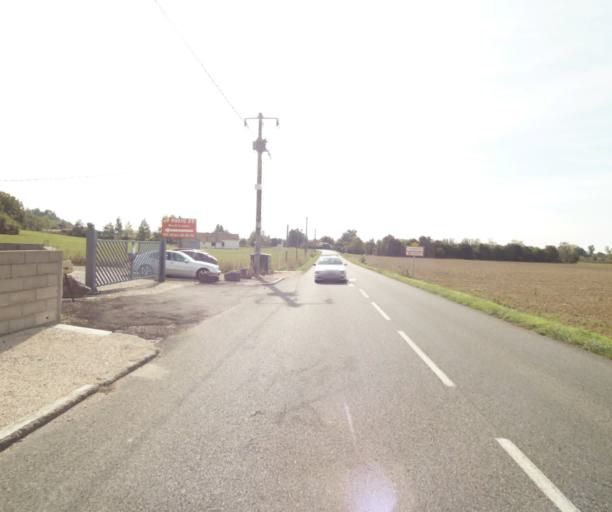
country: FR
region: Midi-Pyrenees
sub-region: Departement du Tarn-et-Garonne
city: Corbarieu
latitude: 43.9514
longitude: 1.3648
